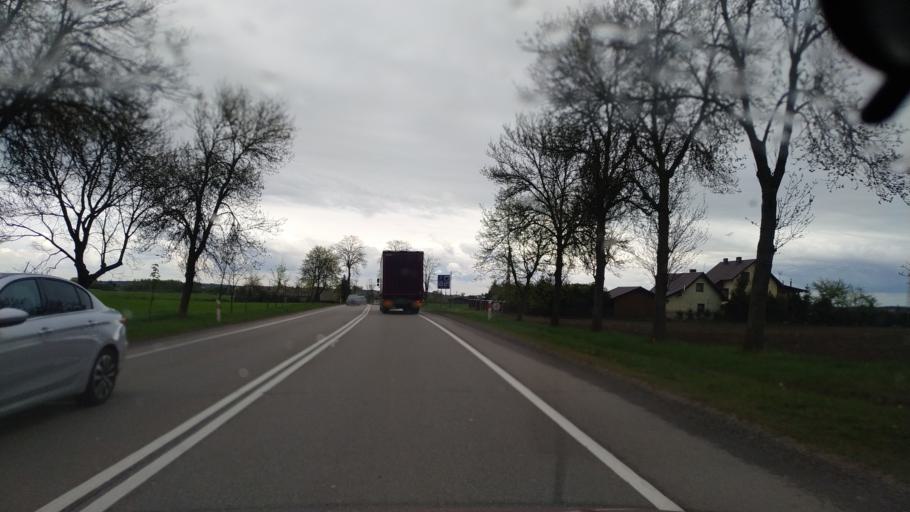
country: PL
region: Pomeranian Voivodeship
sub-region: Powiat starogardzki
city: Zblewo
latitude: 53.9261
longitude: 18.2984
